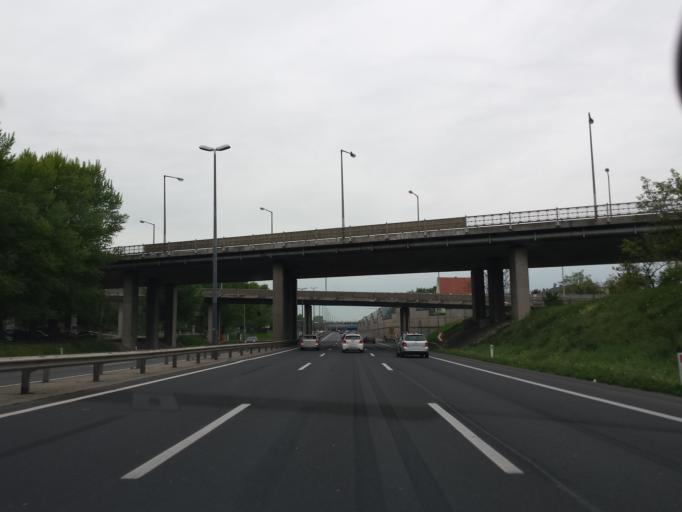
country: AT
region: Vienna
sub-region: Wien Stadt
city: Vienna
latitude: 48.2397
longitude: 16.4030
